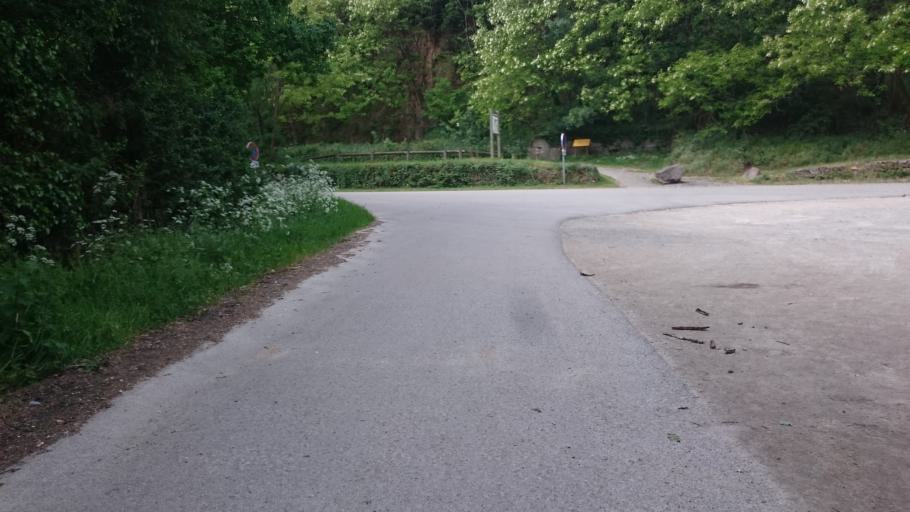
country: FR
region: Pays de la Loire
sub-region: Departement de la Loire-Atlantique
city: Indre
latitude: 47.1837
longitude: -1.6502
